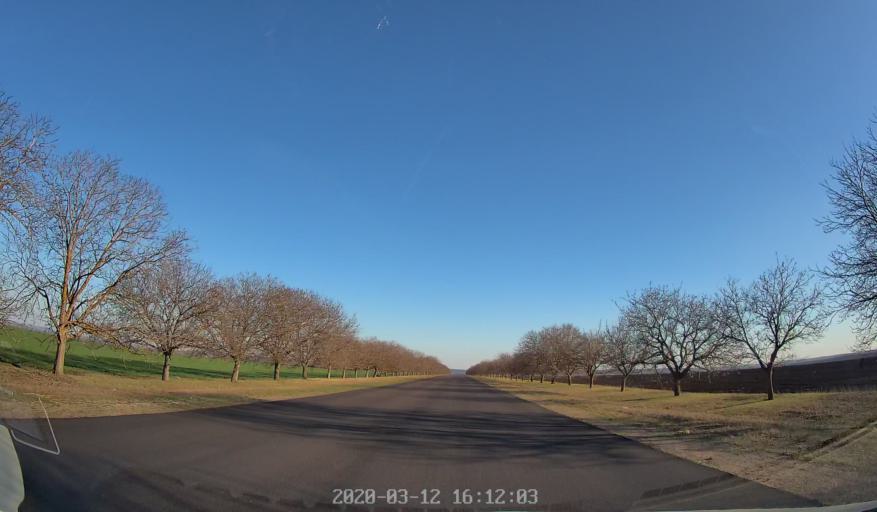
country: MD
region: Anenii Noi
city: Anenii Noi
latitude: 46.9404
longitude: 29.2675
